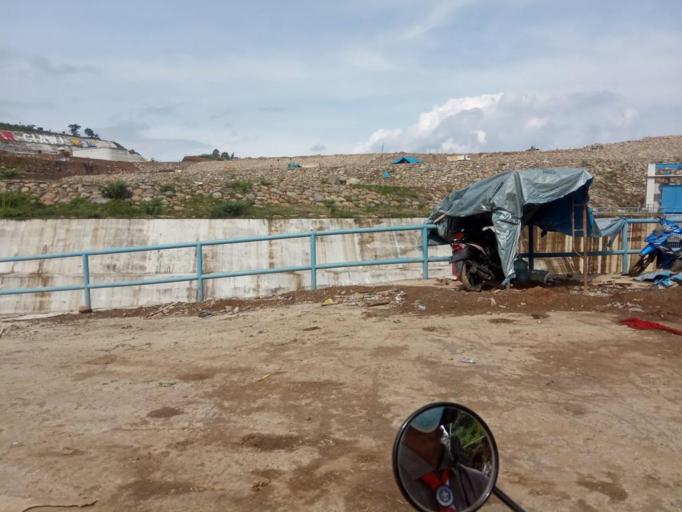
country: ID
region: West Java
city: Caringin
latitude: -6.6569
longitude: 106.8828
